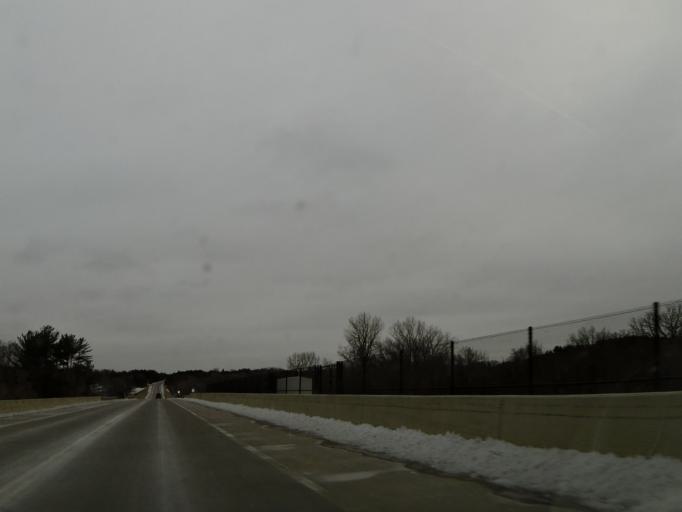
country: US
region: Minnesota
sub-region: Scott County
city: Jordan
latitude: 44.6930
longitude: -93.6423
